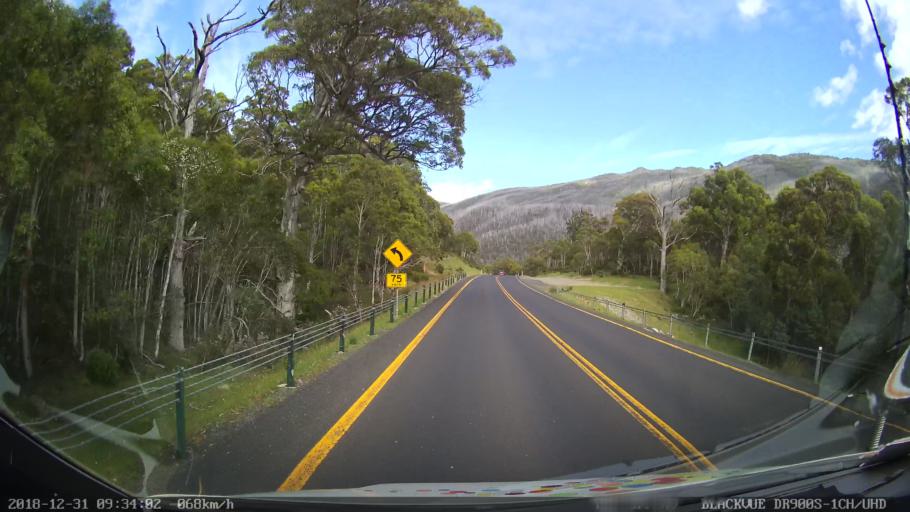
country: AU
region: New South Wales
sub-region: Snowy River
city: Jindabyne
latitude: -36.4500
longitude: 148.4160
